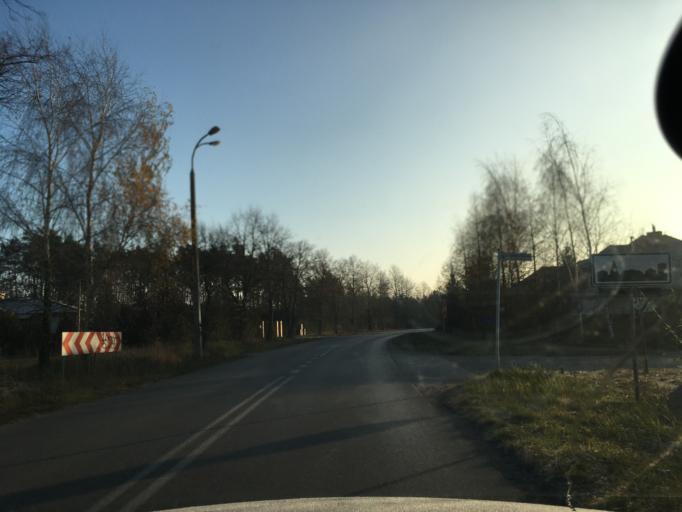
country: PL
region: Masovian Voivodeship
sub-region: Powiat piaseczynski
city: Lesznowola
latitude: 52.0744
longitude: 20.9709
